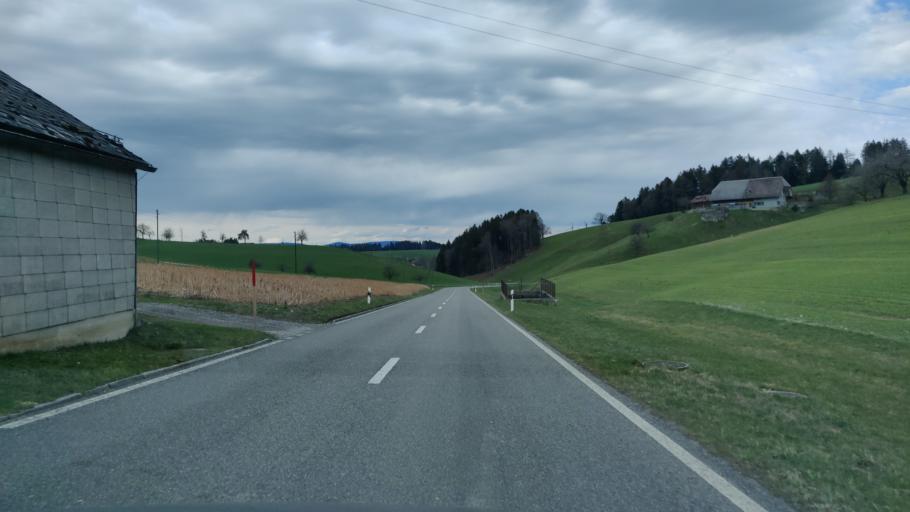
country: CH
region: Bern
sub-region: Emmental District
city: Durrenroth
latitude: 47.0985
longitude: 7.7764
